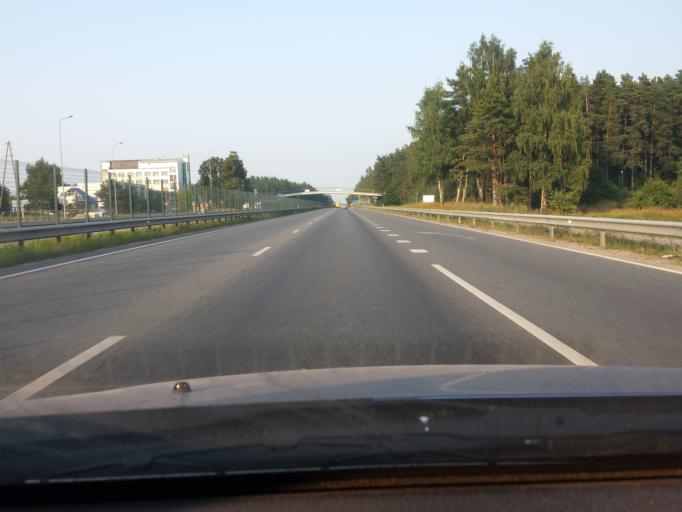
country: LV
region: Riga
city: Bergi
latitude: 57.0034
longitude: 24.2874
